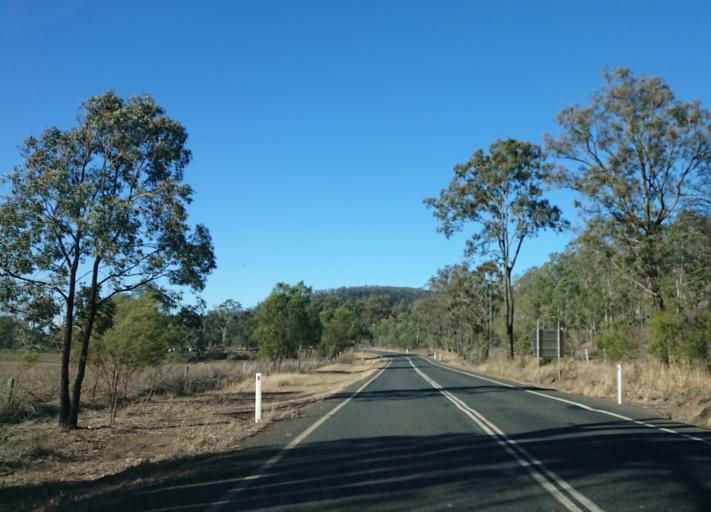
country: AU
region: Queensland
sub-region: Toowoomba
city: Top Camp
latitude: -27.7334
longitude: 152.1083
